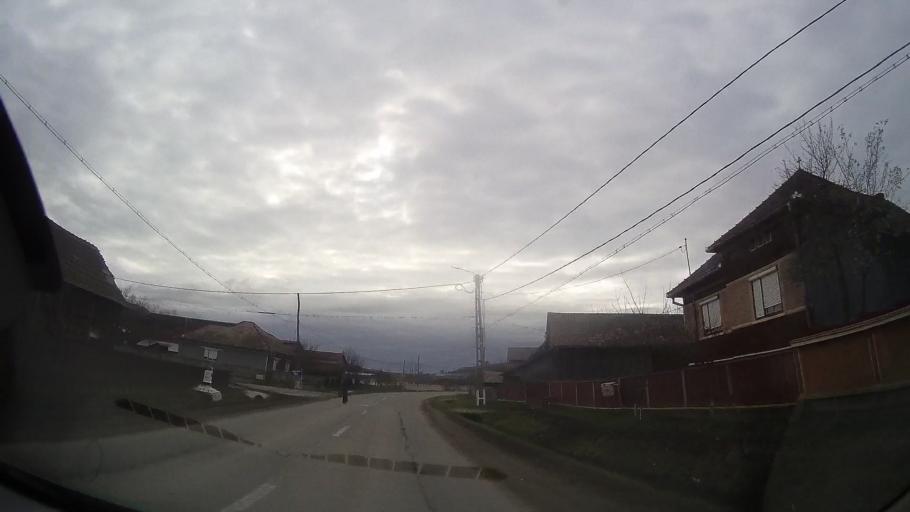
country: RO
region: Bistrita-Nasaud
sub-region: Comuna Budesti
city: Budesti
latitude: 46.8728
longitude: 24.2466
